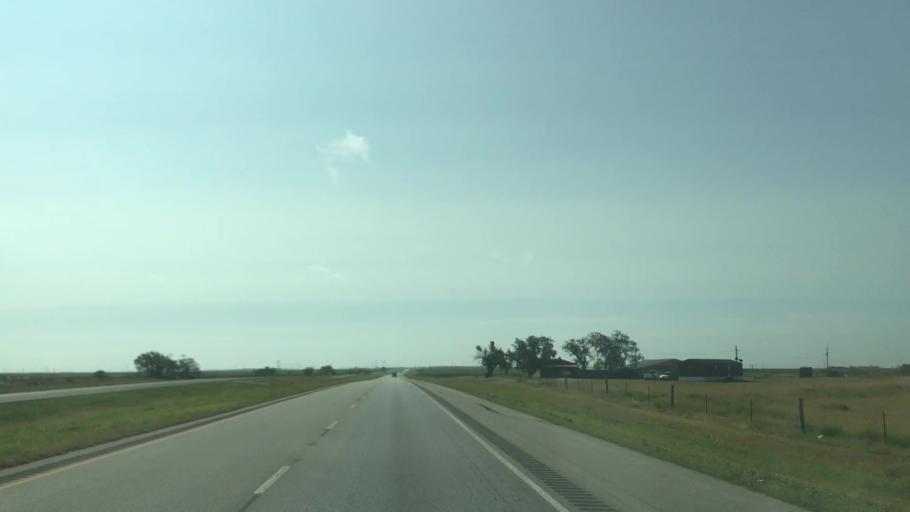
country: US
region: Texas
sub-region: Scurry County
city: Snyder
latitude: 32.6710
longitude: -100.8019
